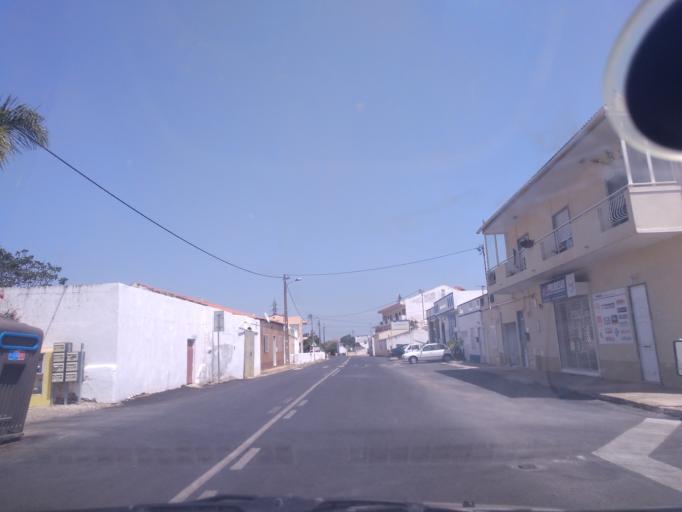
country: PT
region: Faro
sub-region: Faro
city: Faro
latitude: 37.0519
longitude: -7.9426
